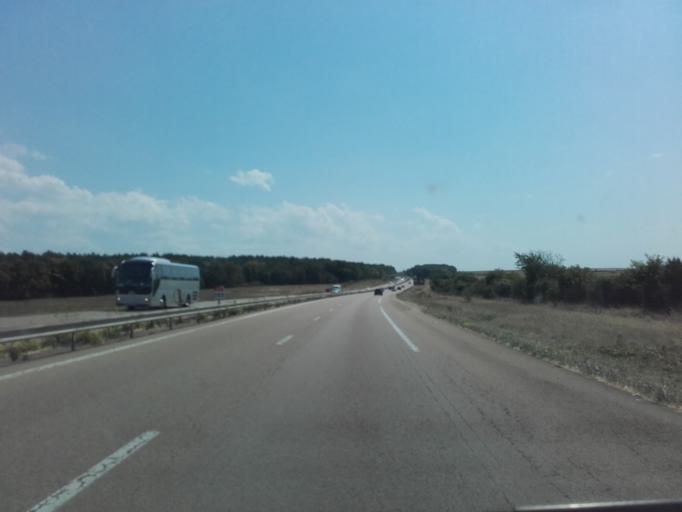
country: FR
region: Bourgogne
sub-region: Departement de l'Yonne
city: Joux-la-Ville
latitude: 47.6425
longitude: 3.9071
